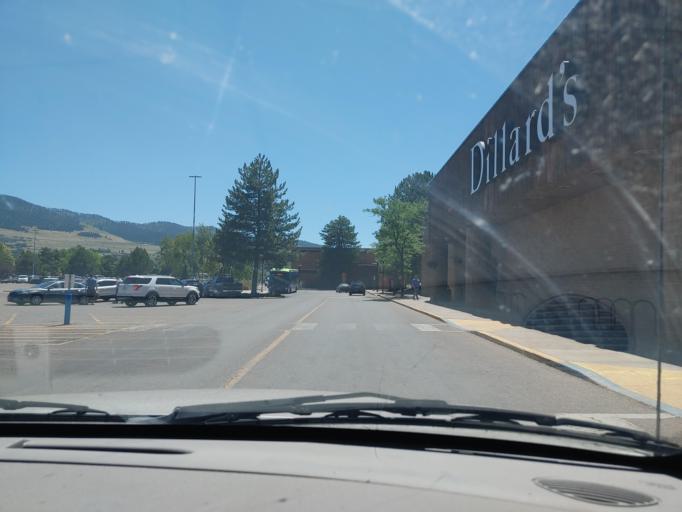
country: US
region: Montana
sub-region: Missoula County
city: Orchard Homes
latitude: 46.8475
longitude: -114.0265
